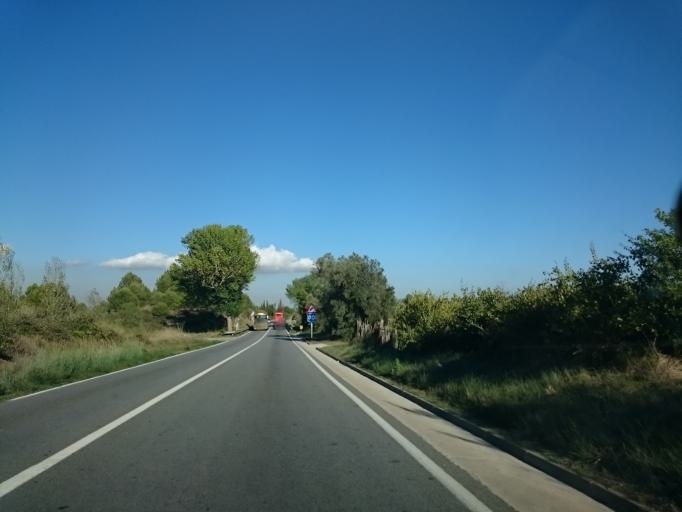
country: ES
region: Catalonia
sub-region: Provincia de Barcelona
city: Castellvi de Rosanes
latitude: 41.4790
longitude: 1.8883
